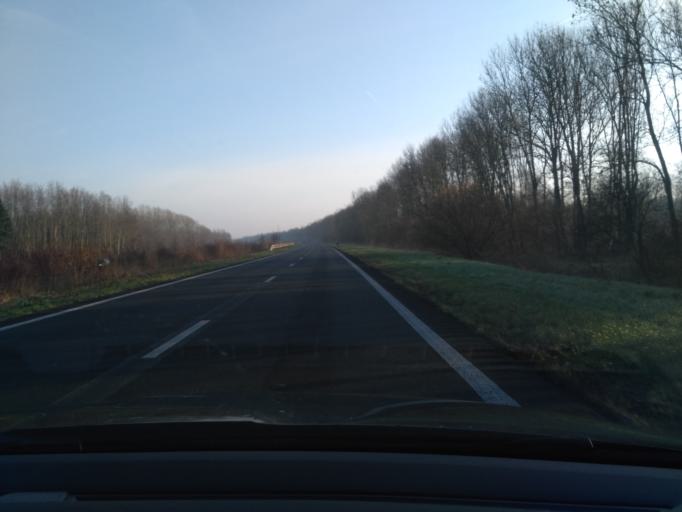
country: NL
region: Flevoland
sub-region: Gemeente Zeewolde
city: Zeewolde
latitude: 52.3307
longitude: 5.4711
